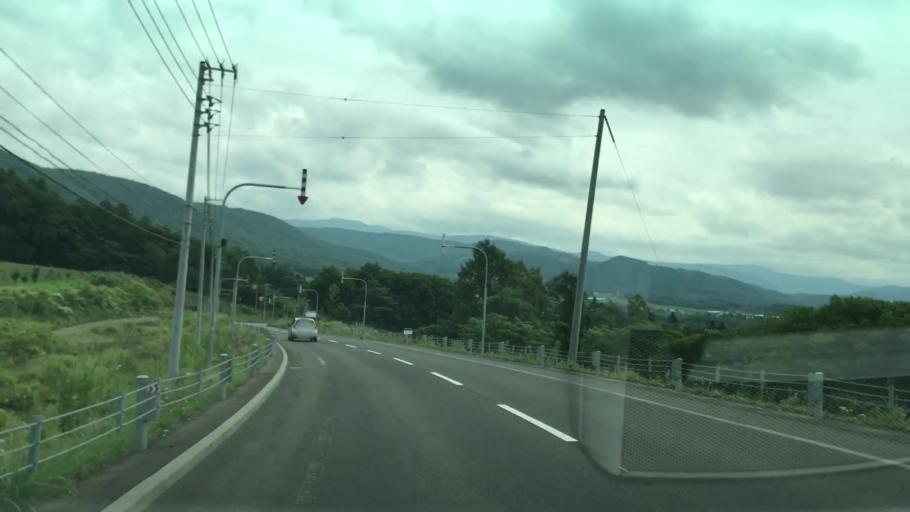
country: JP
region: Hokkaido
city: Yoichi
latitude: 43.1091
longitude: 140.8202
